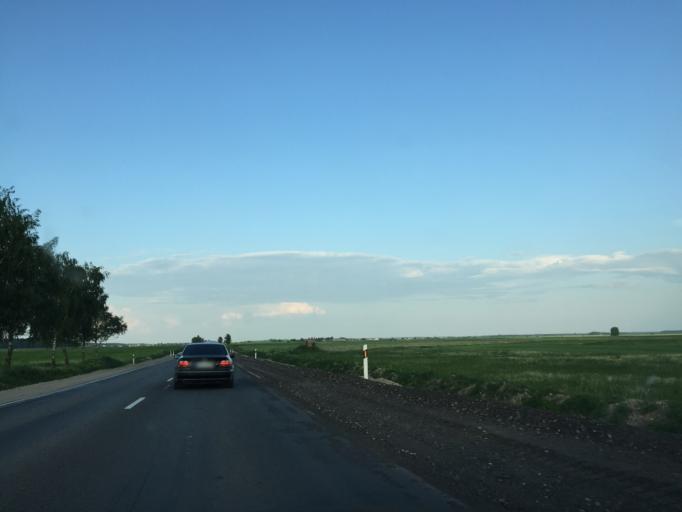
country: LT
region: Telsiu apskritis
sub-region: Telsiai
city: Telsiai
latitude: 56.0045
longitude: 22.3241
